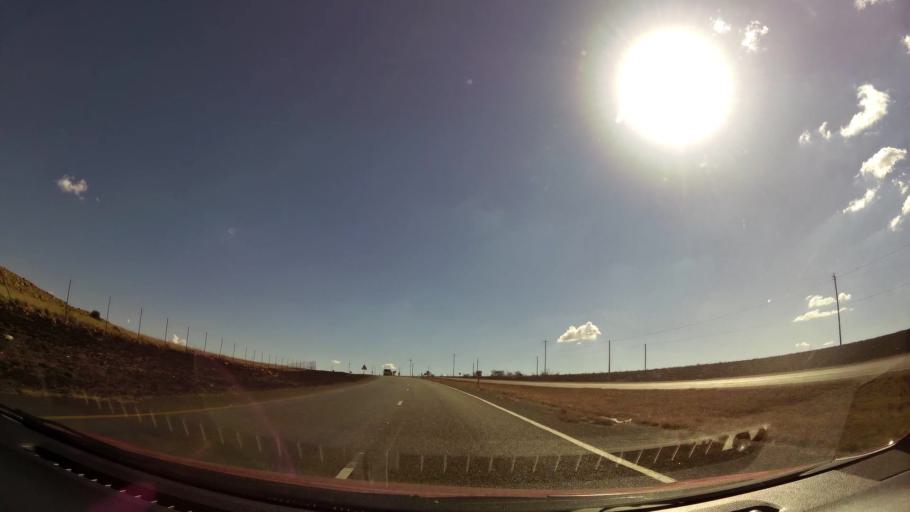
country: ZA
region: Gauteng
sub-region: West Rand District Municipality
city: Carletonville
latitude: -26.4161
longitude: 27.4542
